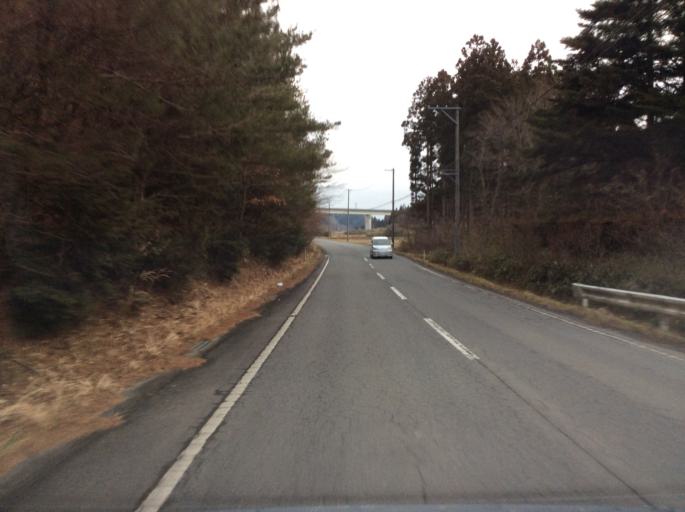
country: JP
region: Fukushima
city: Iwaki
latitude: 37.1368
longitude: 140.9507
